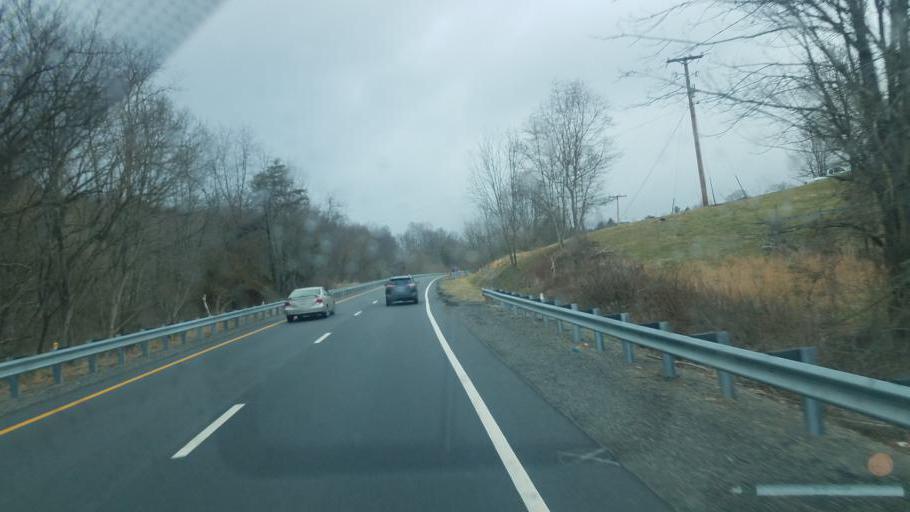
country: US
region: Virginia
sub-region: Giles County
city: Pearisburg
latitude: 37.2927
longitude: -80.7411
